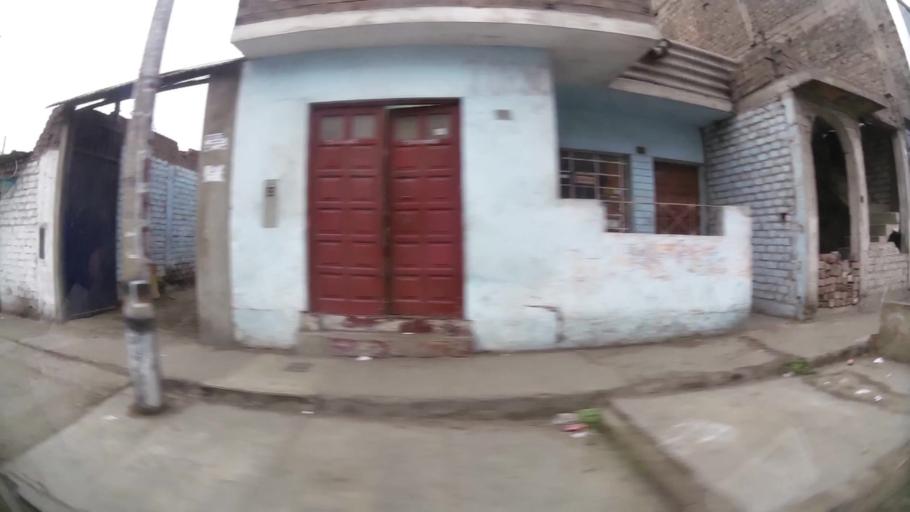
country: PE
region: Lima
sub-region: Lima
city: Surco
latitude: -12.1519
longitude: -76.9750
